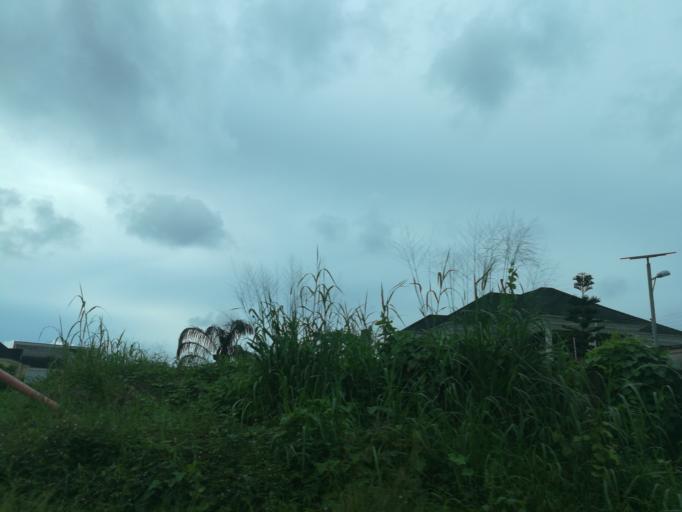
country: NG
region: Rivers
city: Port Harcourt
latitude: 4.8175
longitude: 6.9907
